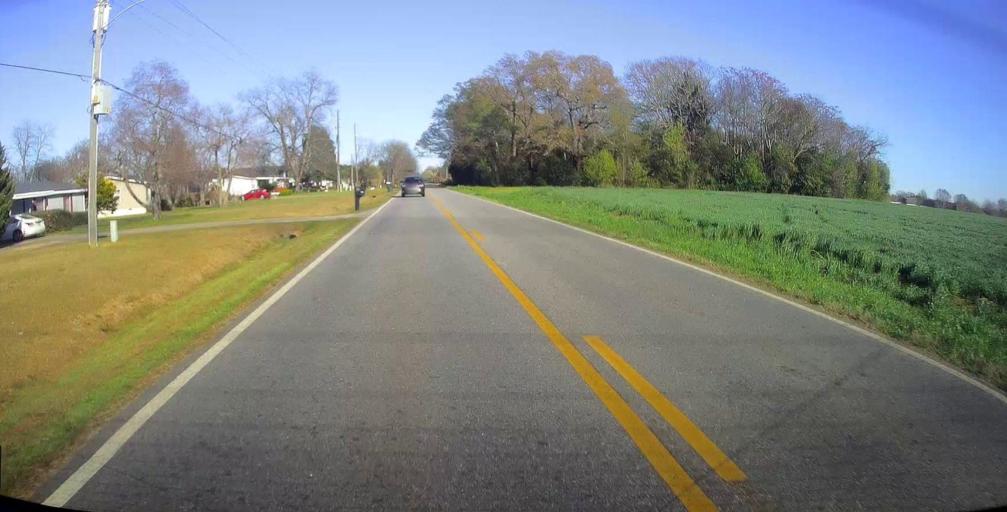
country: US
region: Georgia
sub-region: Houston County
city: Centerville
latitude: 32.6349
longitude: -83.7261
